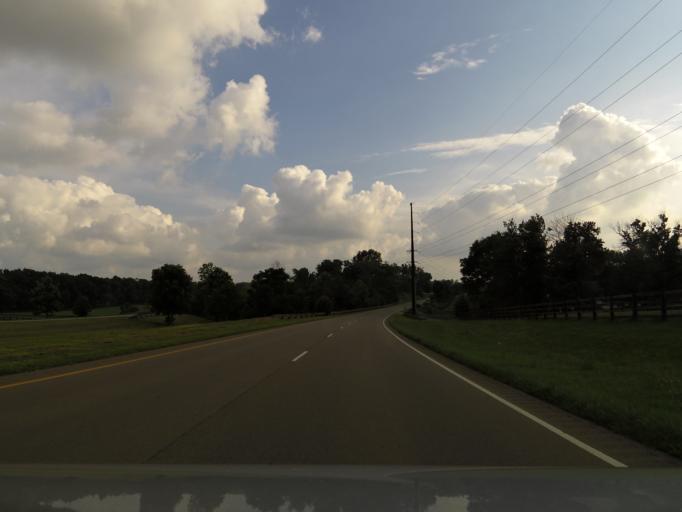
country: US
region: Kentucky
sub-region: Bourbon County
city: Paris
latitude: 38.1714
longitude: -84.3107
